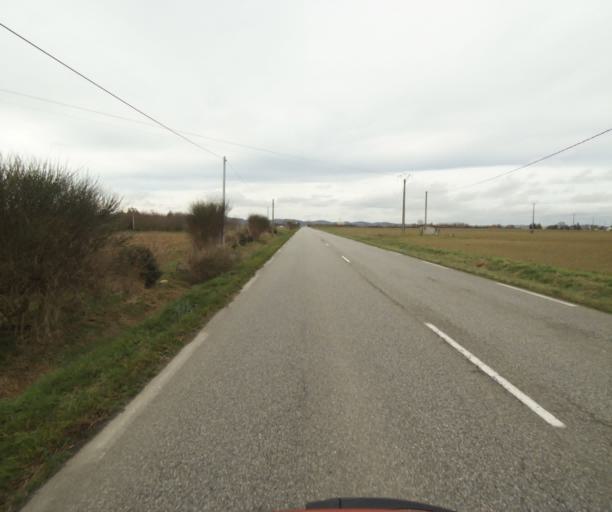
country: FR
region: Midi-Pyrenees
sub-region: Departement de l'Ariege
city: La Tour-du-Crieu
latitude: 43.0946
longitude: 1.6690
